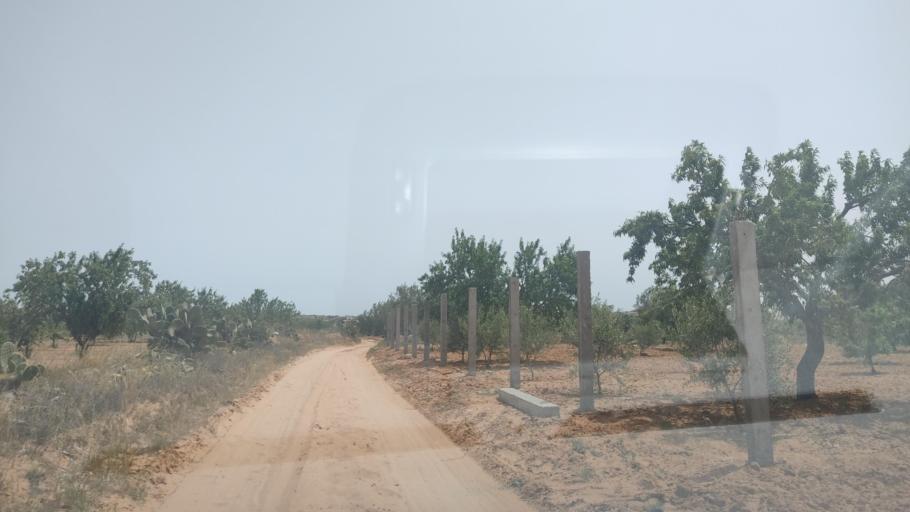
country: TN
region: Safaqis
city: Sfax
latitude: 34.8352
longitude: 10.5990
